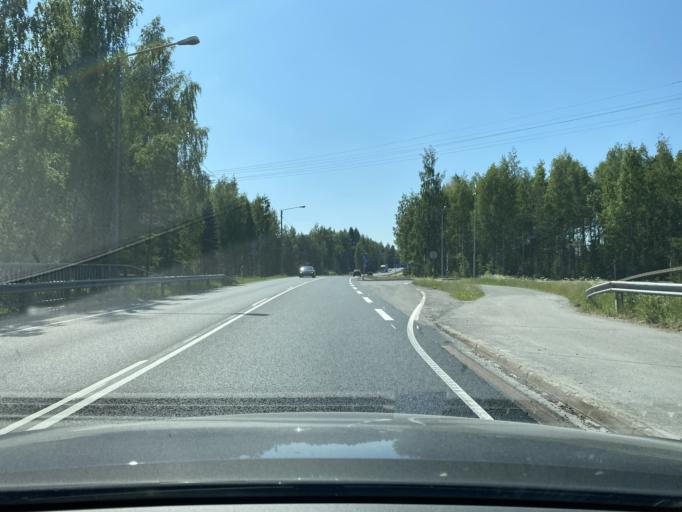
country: FI
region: Pirkanmaa
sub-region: Tampere
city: Nokia
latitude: 61.4637
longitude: 23.5047
